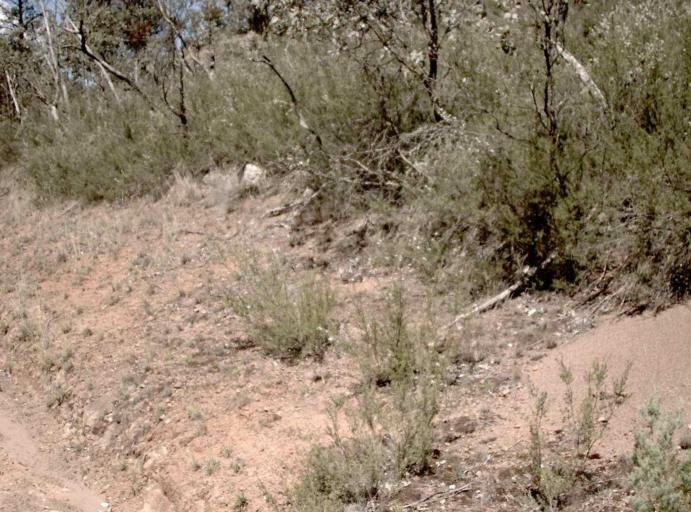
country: AU
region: New South Wales
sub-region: Snowy River
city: Jindabyne
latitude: -37.0627
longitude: 148.5047
